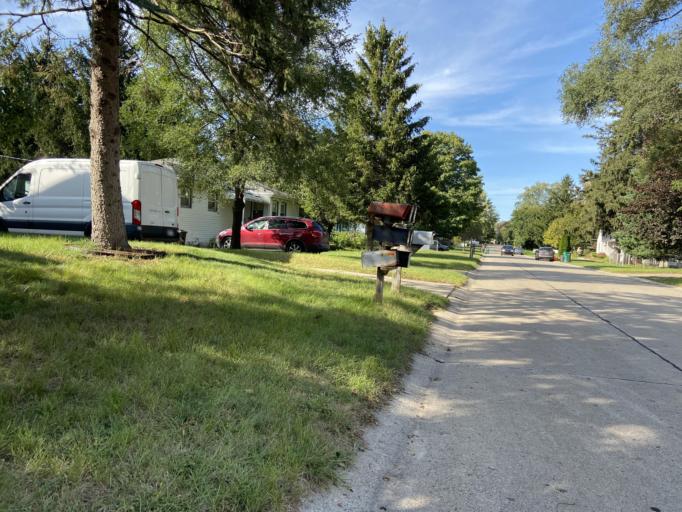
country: US
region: Michigan
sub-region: Oakland County
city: Farmington
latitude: 42.4475
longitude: -83.3196
